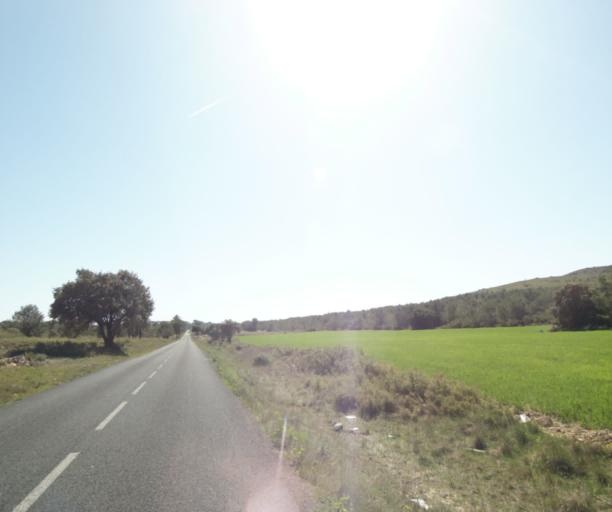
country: FR
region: Languedoc-Roussillon
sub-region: Departement de l'Herault
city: Saint-Drezery
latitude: 43.7328
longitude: 3.9570
